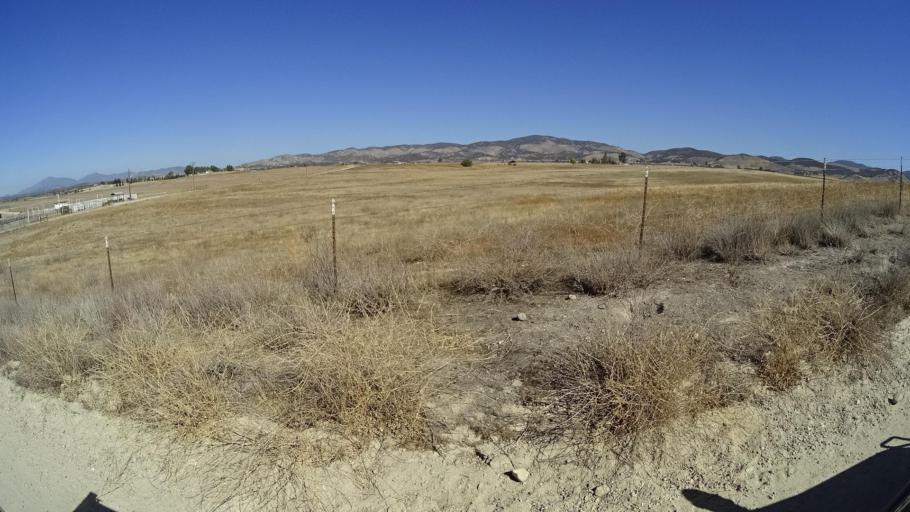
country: US
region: California
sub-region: Monterey County
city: King City
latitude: 35.9513
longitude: -121.0990
